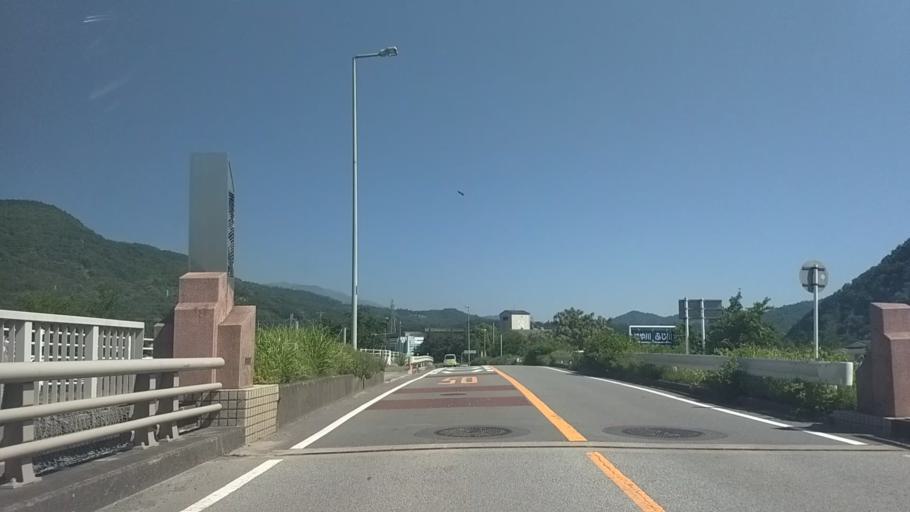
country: JP
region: Yamanashi
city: Ryuo
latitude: 35.4303
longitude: 138.4435
